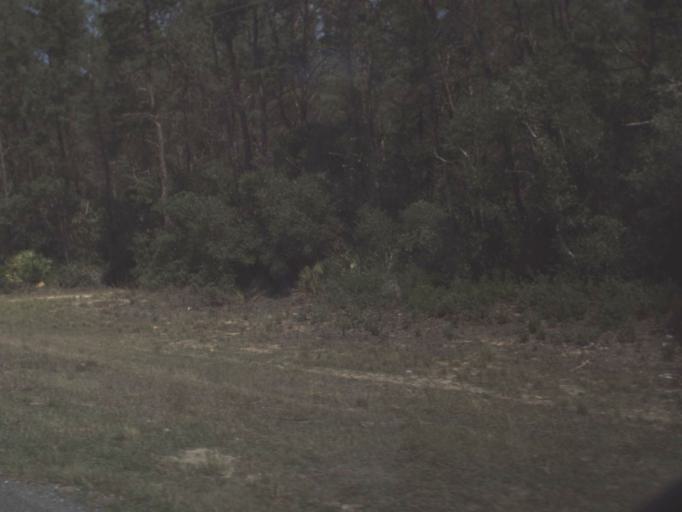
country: US
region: Florida
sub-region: Marion County
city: Silver Springs Shores
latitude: 29.1768
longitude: -81.8045
